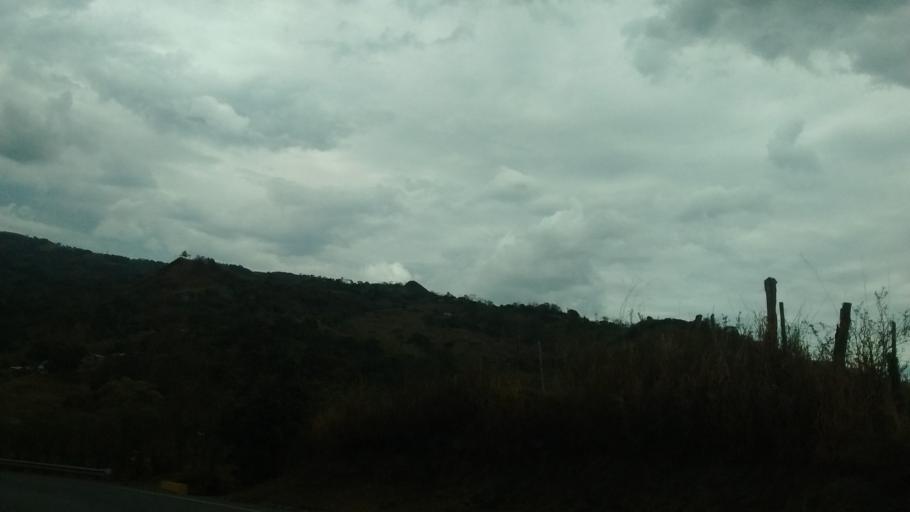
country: CO
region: Cauca
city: Rosas
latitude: 2.2802
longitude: -76.7080
